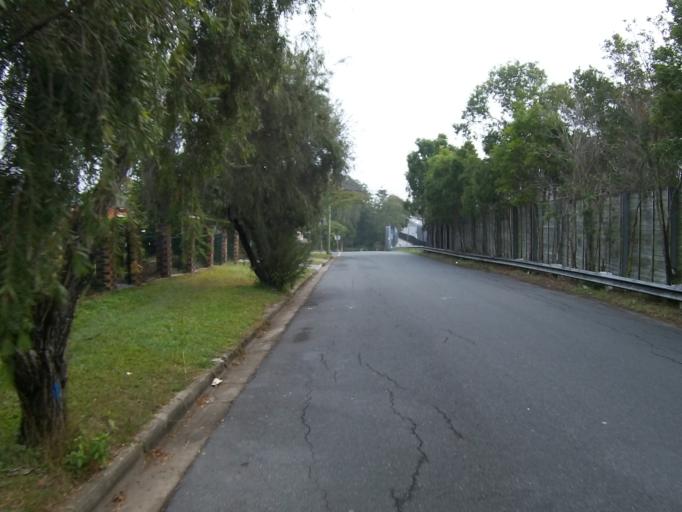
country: AU
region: Queensland
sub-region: Brisbane
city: Nathan
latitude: -27.5545
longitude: 153.0701
